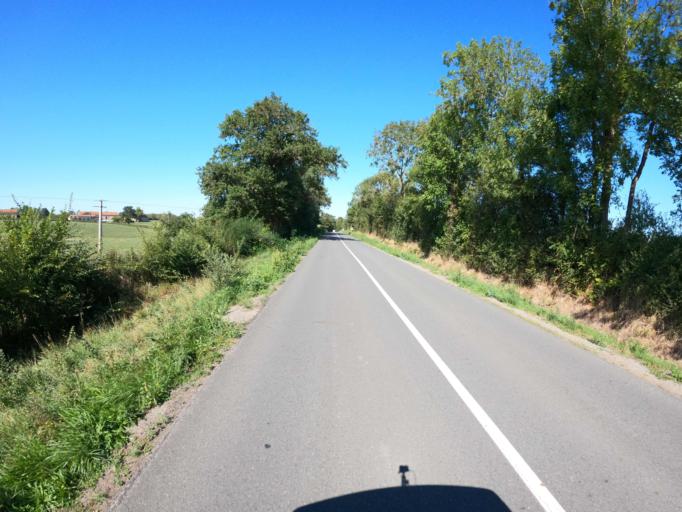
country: FR
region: Poitou-Charentes
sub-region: Departement de la Vienne
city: Lathus-Saint-Remy
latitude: 46.3491
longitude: 0.9483
